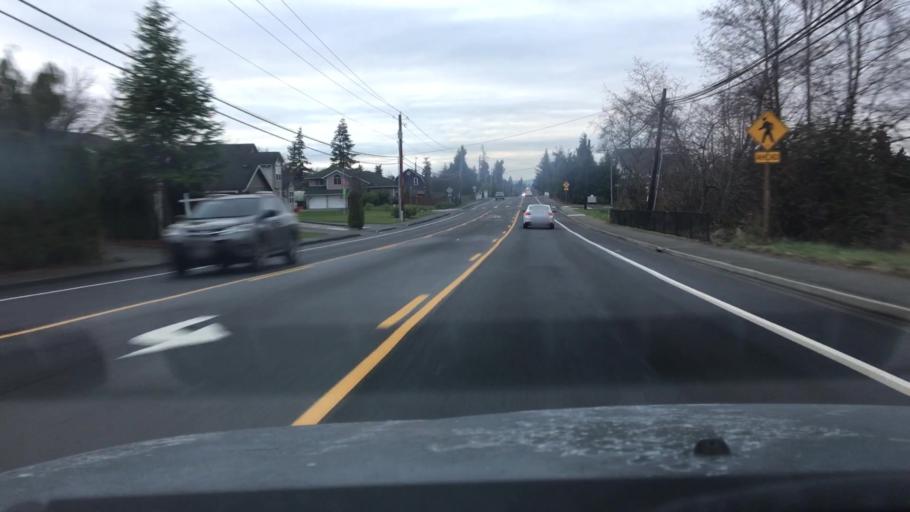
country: US
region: Washington
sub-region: Skagit County
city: Mount Vernon
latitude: 48.4209
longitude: -122.2994
